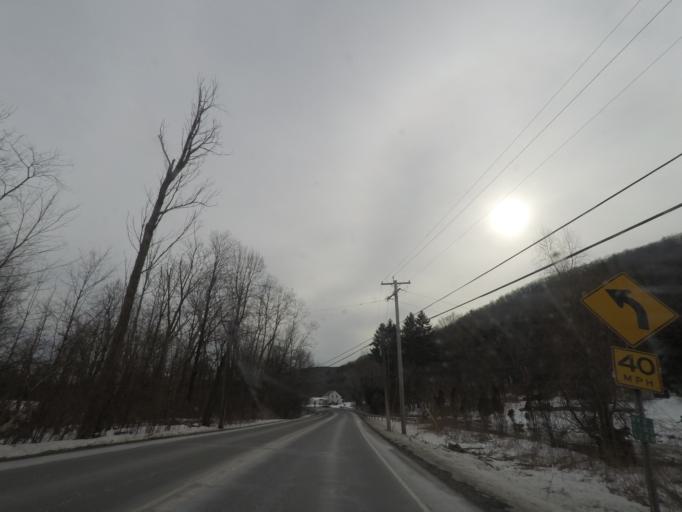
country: US
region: New York
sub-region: Albany County
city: Voorheesville
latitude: 42.5877
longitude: -73.9832
